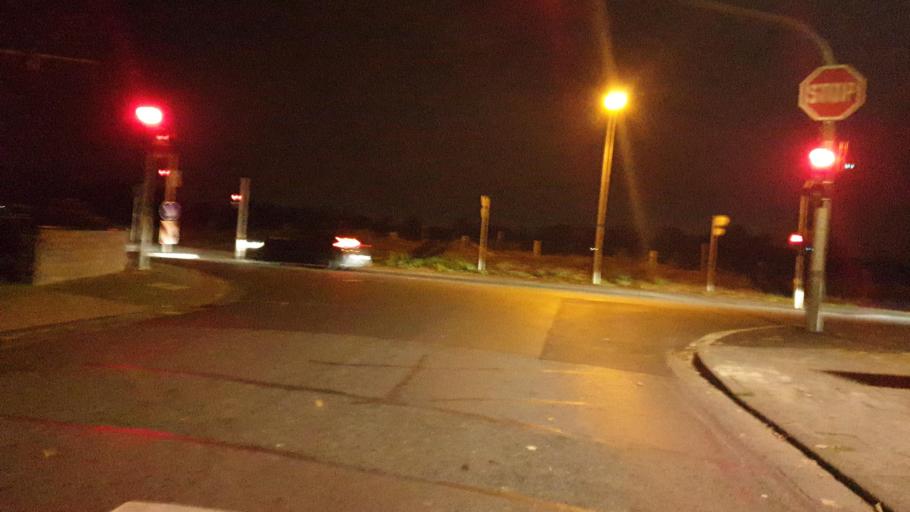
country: DE
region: North Rhine-Westphalia
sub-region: Regierungsbezirk Koln
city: Kerpen
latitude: 50.9118
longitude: 6.6890
